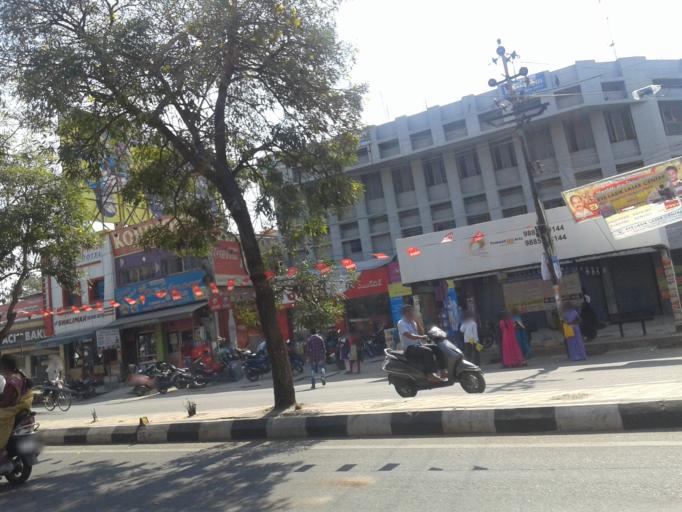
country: IN
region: Telangana
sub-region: Warangal
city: Warangal
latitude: 17.9884
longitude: 79.6008
